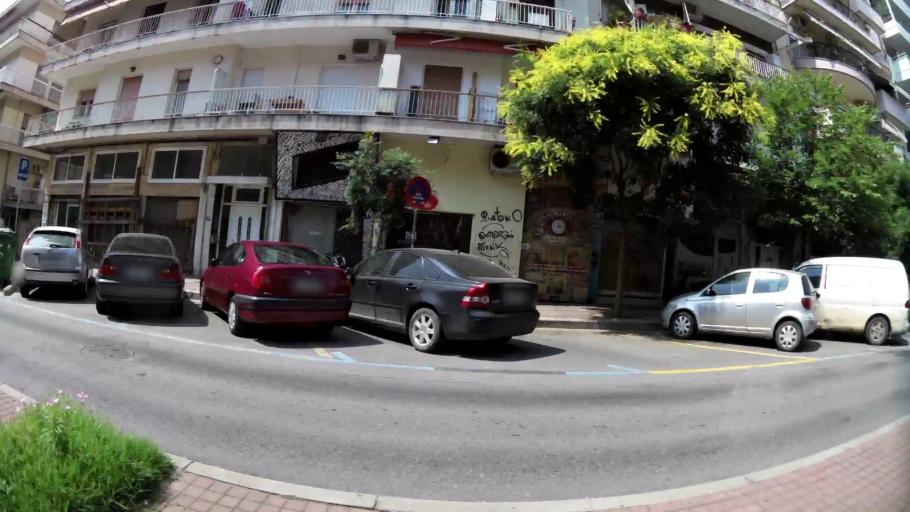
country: GR
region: Central Macedonia
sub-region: Nomos Thessalonikis
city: Sykies
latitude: 40.6400
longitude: 22.9507
